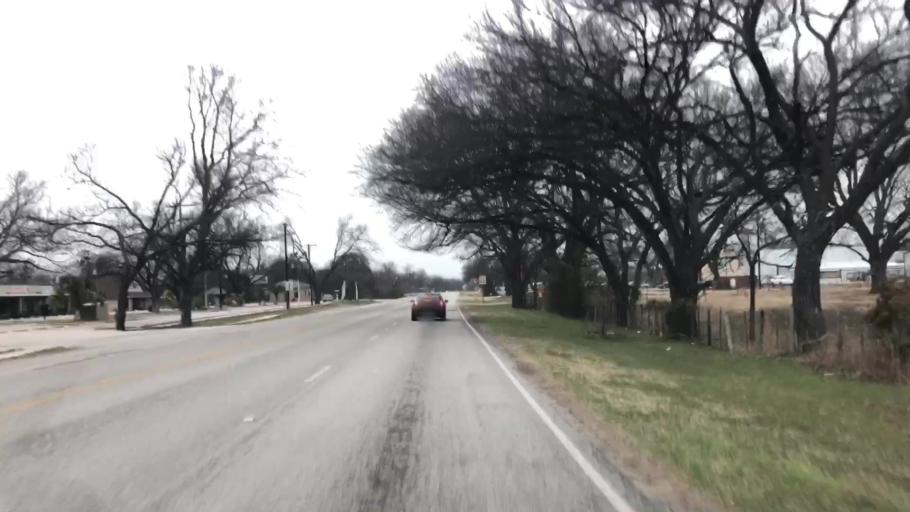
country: US
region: Texas
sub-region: Lampasas County
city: Lampasas
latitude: 31.0456
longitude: -98.1807
